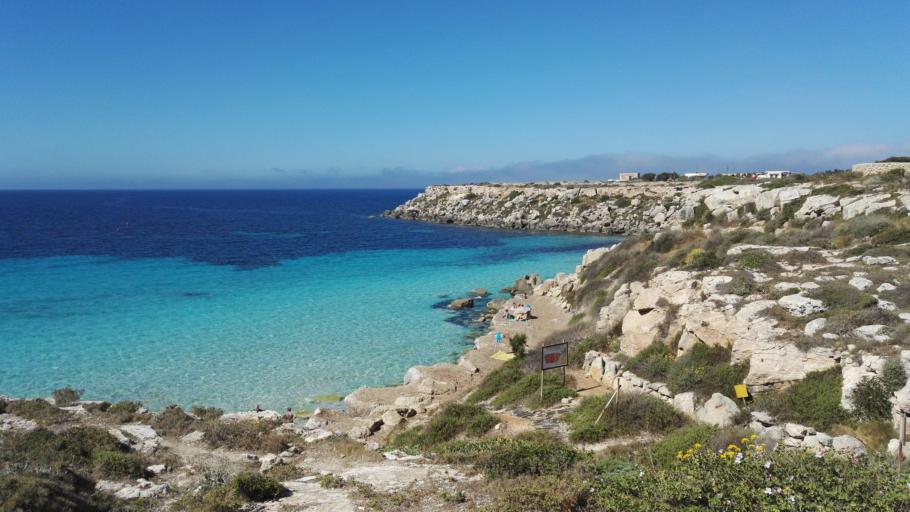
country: IT
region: Sicily
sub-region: Trapani
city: Favignana
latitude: 37.9094
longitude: 12.3619
